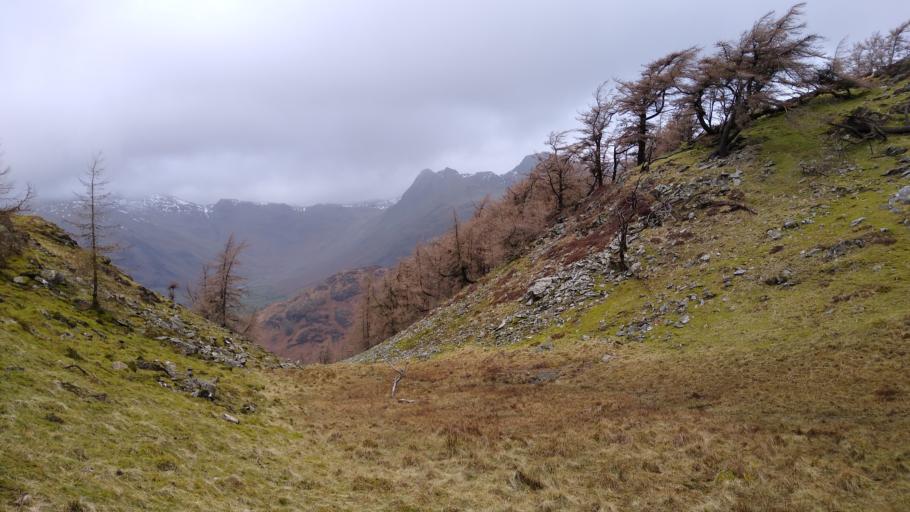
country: GB
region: England
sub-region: Cumbria
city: Ambleside
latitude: 54.4307
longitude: -3.0790
